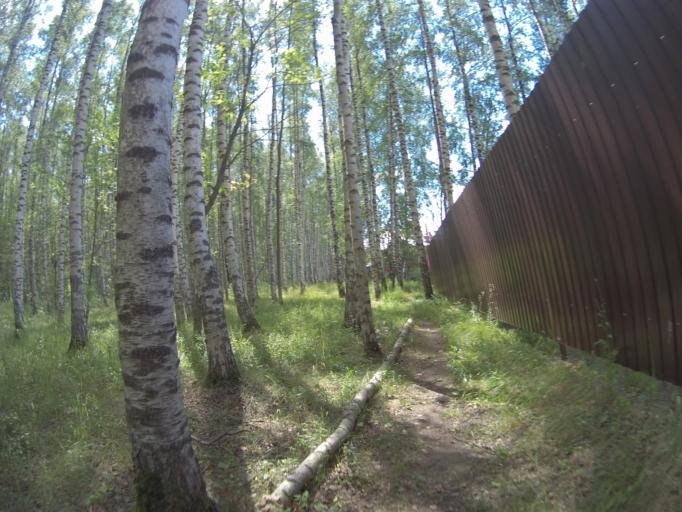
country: RU
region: Vladimir
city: Kommunar
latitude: 56.0592
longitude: 40.5020
